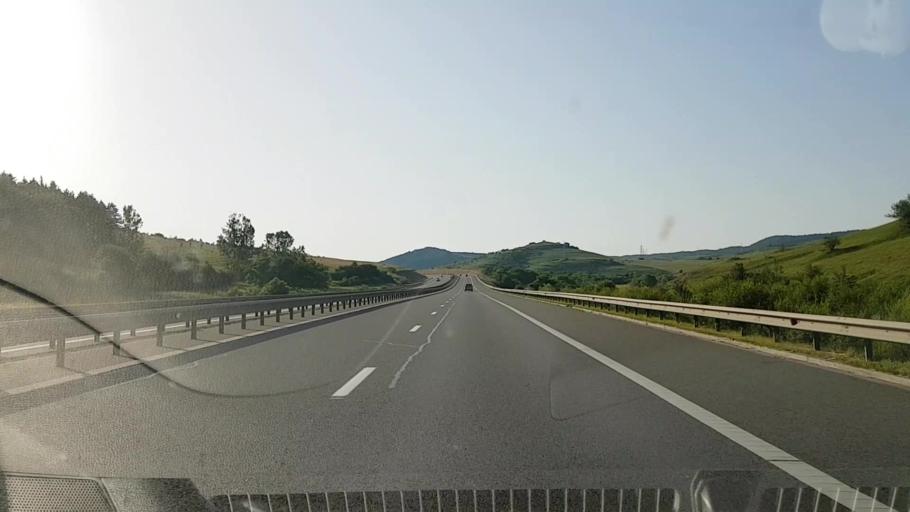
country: RO
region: Cluj
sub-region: Comuna Savadisla
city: Savadisla
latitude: 46.6815
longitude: 23.4733
